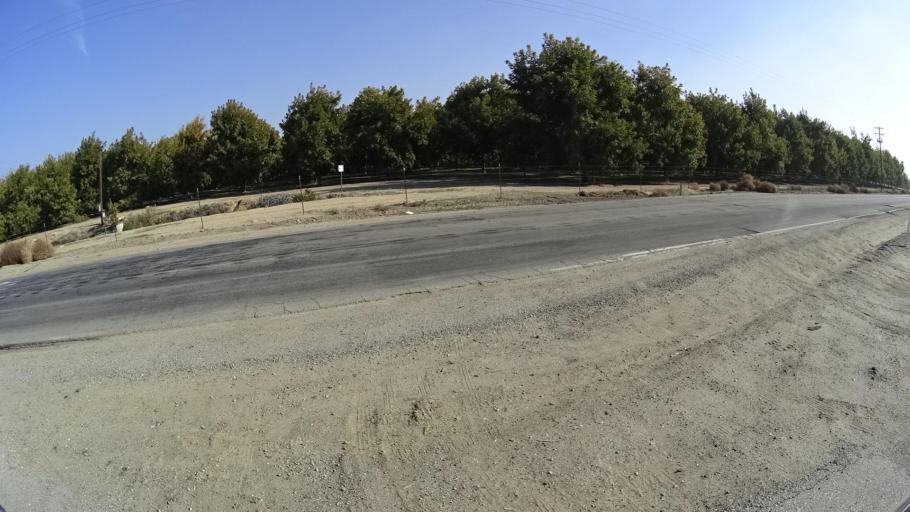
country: US
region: California
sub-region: Kern County
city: McFarland
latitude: 35.6363
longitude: -119.2046
